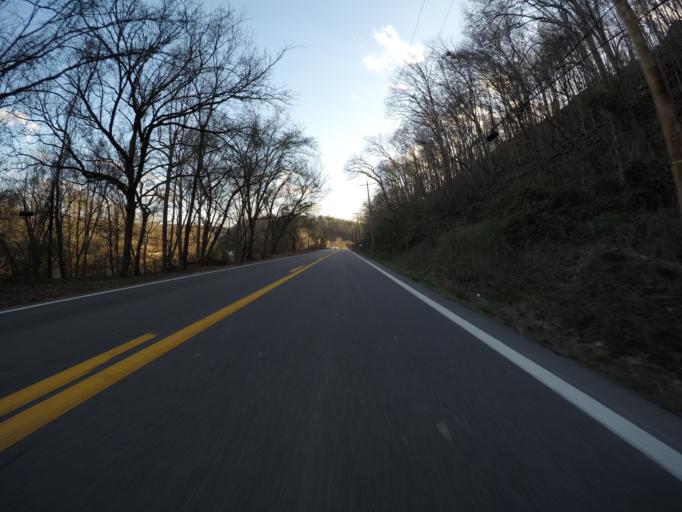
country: US
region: West Virginia
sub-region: Kanawha County
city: Charleston
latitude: 38.3968
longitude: -81.5855
